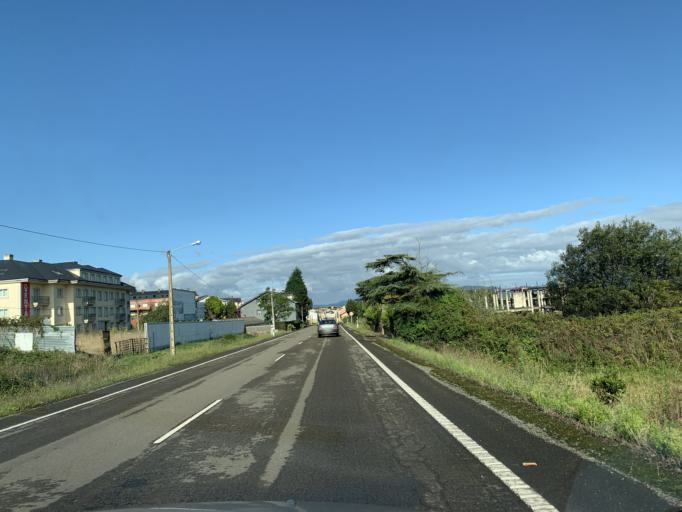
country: ES
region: Galicia
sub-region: Provincia de Lugo
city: Barreiros
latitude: 43.5432
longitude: -7.1829
